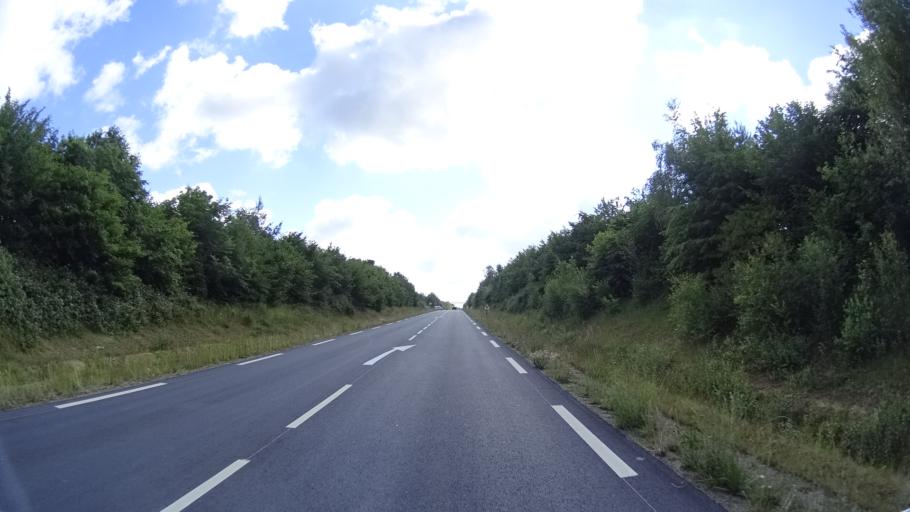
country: FR
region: Brittany
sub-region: Departement d'Ille-et-Vilaine
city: Saint-Gilles
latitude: 48.1308
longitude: -1.8204
